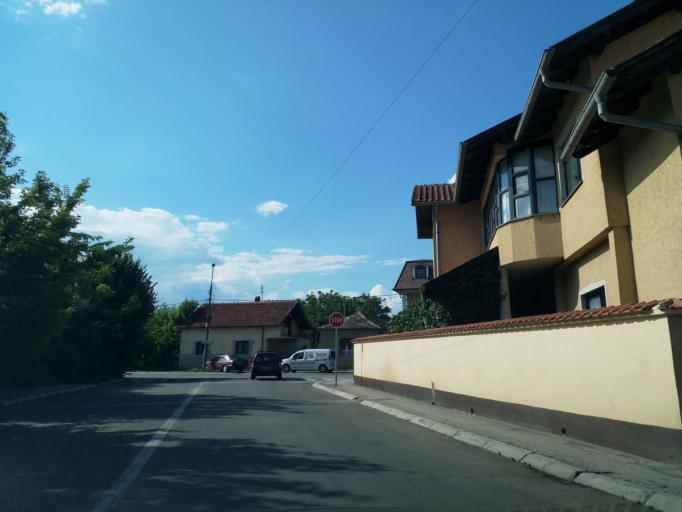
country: RS
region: Central Serbia
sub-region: Pomoravski Okrug
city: Paracin
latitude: 43.8611
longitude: 21.4031
